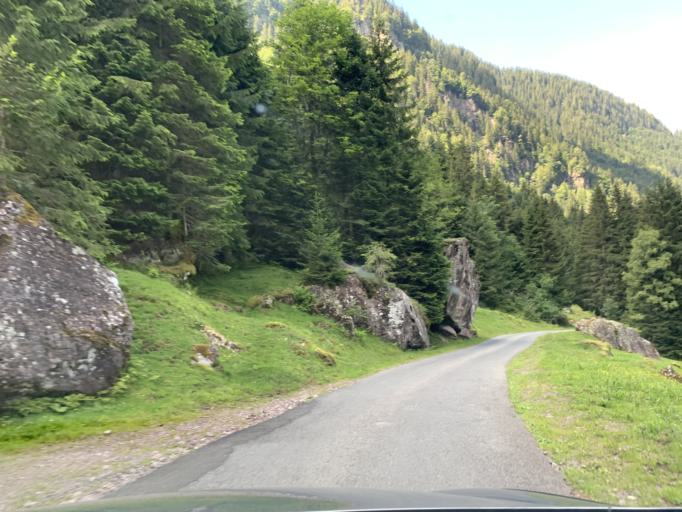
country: CH
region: Saint Gallen
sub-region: Wahlkreis Sarganserland
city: Quarten
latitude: 47.0795
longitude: 9.1985
